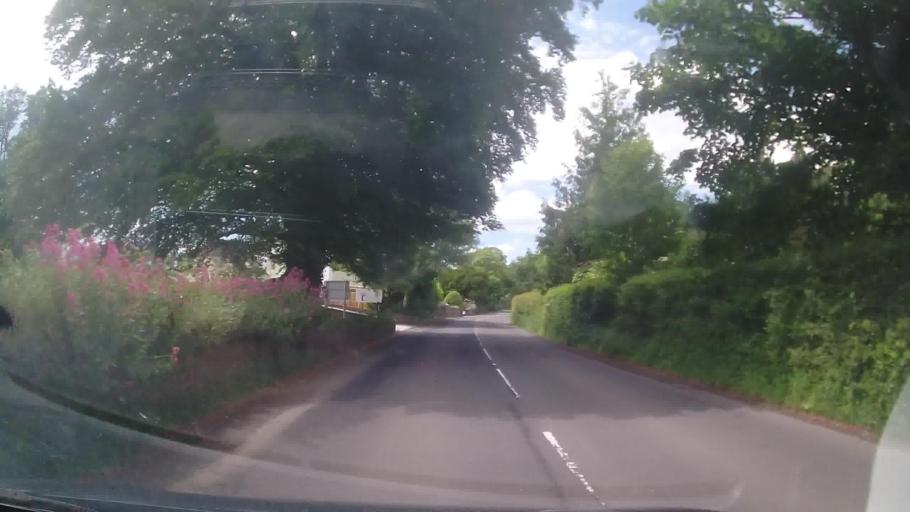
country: GB
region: England
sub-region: Devon
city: Modbury
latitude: 50.3613
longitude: -3.9110
